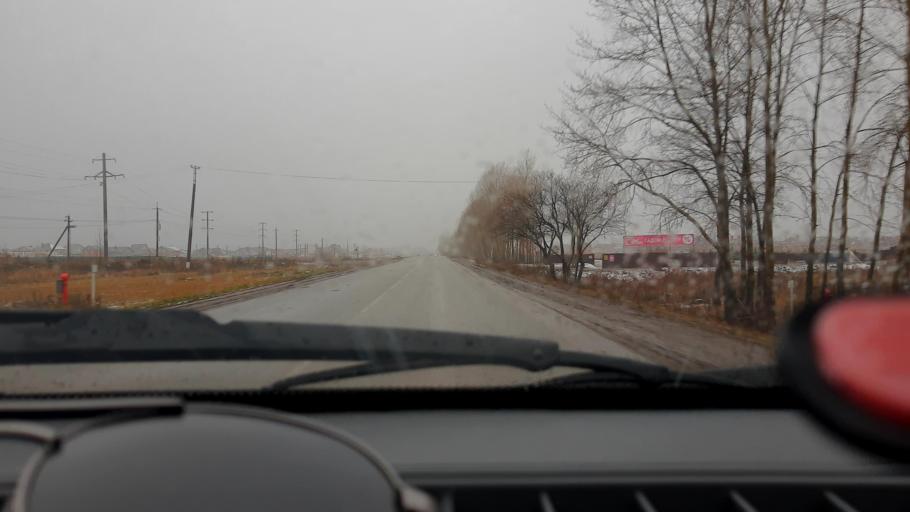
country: RU
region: Bashkortostan
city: Kabakovo
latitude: 54.6148
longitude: 56.1463
